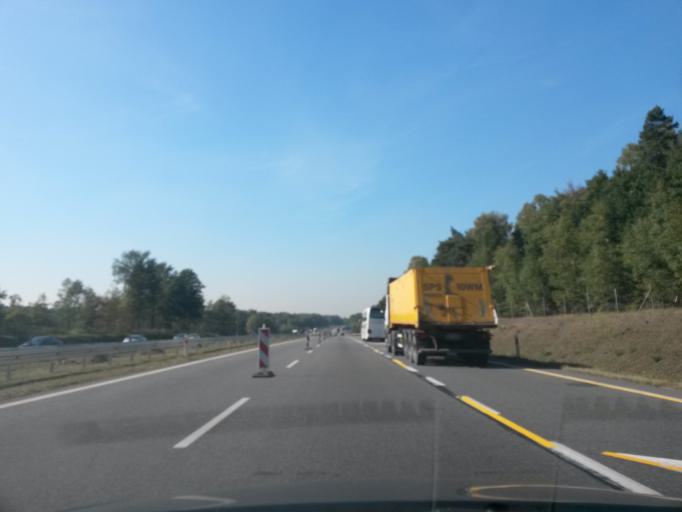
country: PL
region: Silesian Voivodeship
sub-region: Myslowice
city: Myslowice
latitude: 50.2181
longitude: 19.1184
